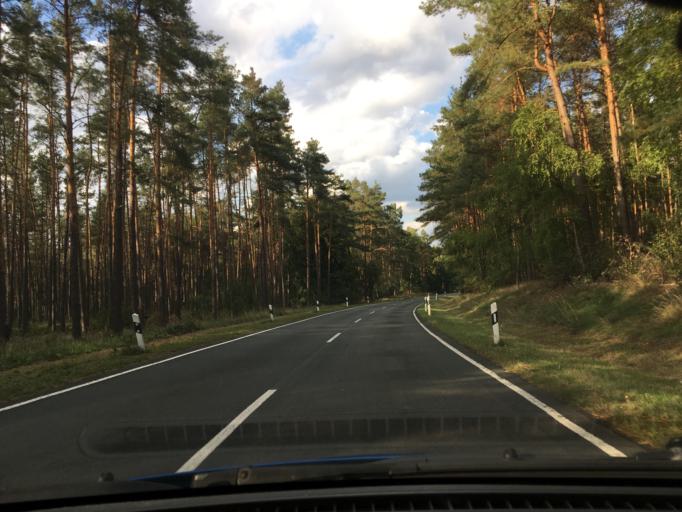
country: DE
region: Lower Saxony
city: Salzhausen
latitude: 53.2512
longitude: 10.1676
